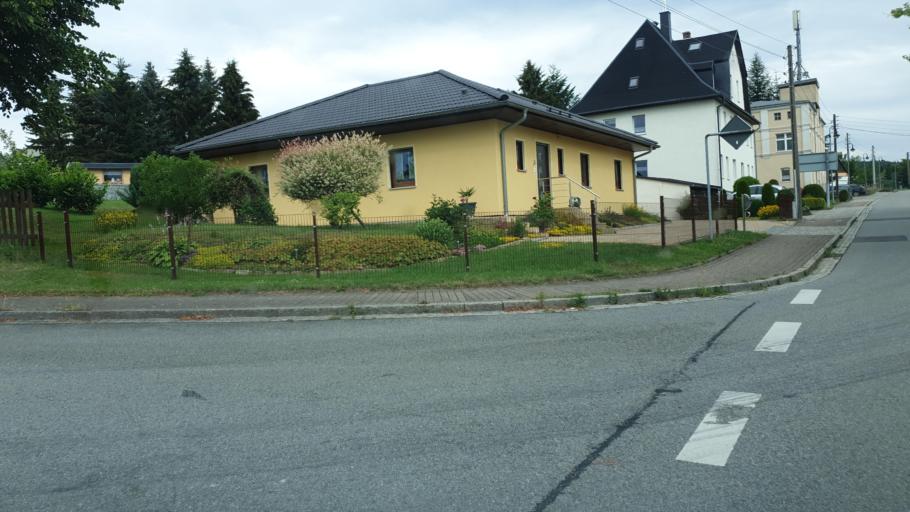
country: DE
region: Saxony
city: Elterlein
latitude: 50.5804
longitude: 12.8654
